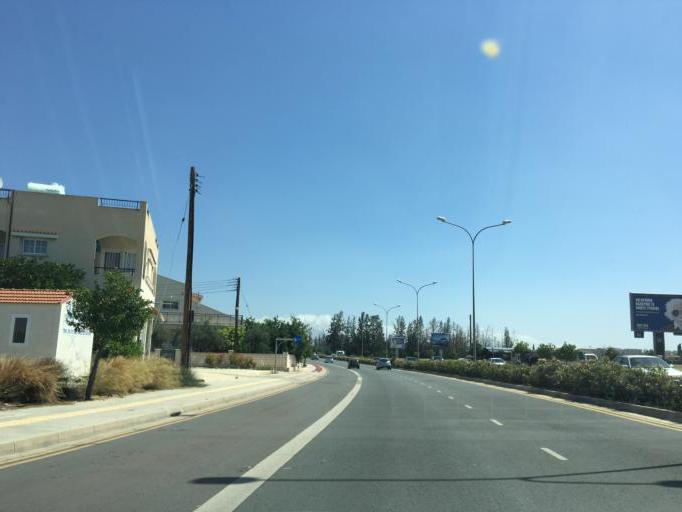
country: CY
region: Lefkosia
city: Nicosia
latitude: 35.1487
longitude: 33.3258
